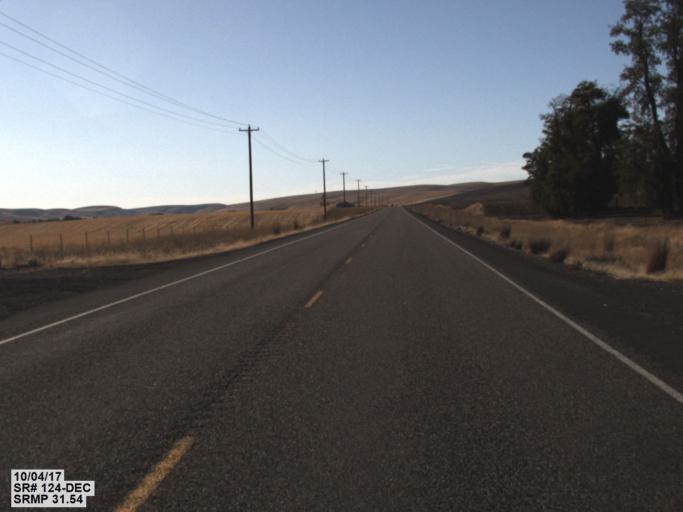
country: US
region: Washington
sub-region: Walla Walla County
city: Walla Walla
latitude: 46.2993
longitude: -118.4101
